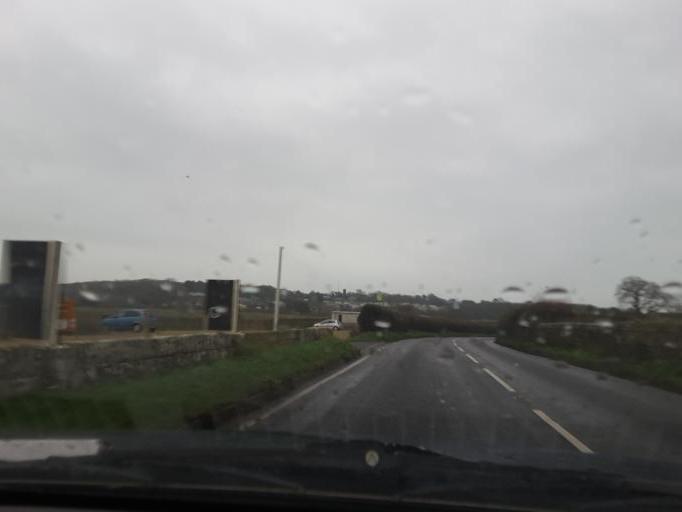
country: GB
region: England
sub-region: Isle of Wight
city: Bembridge
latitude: 50.6757
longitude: -1.1067
